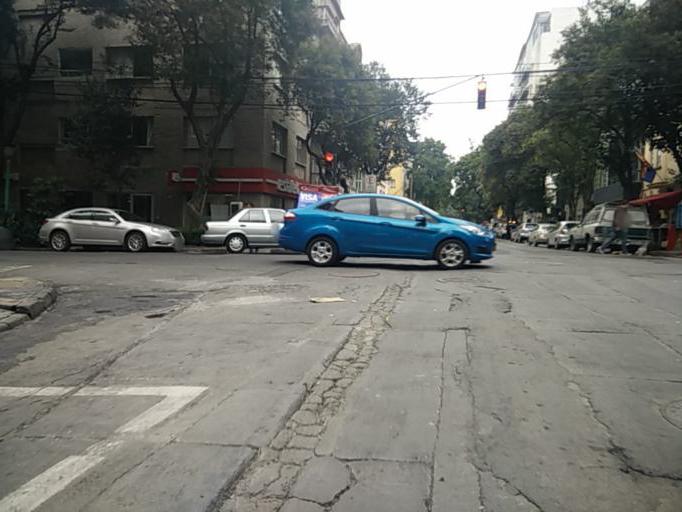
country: MX
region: Mexico City
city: Benito Juarez
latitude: 19.4241
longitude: -99.1693
